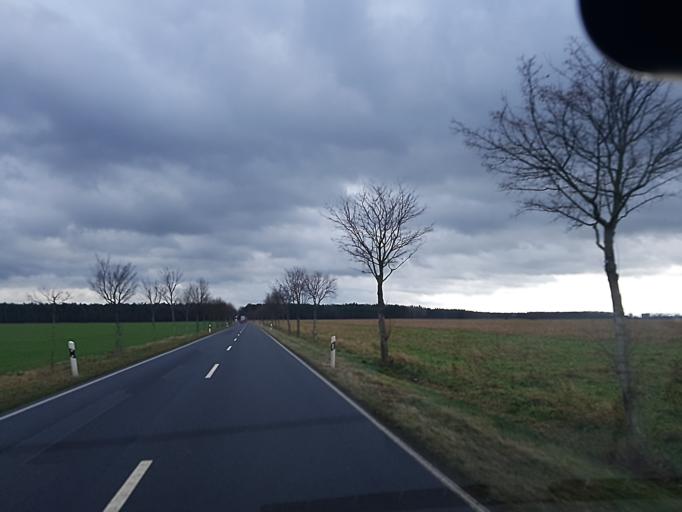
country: DE
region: Brandenburg
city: Bad Liebenwerda
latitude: 51.4950
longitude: 13.3902
